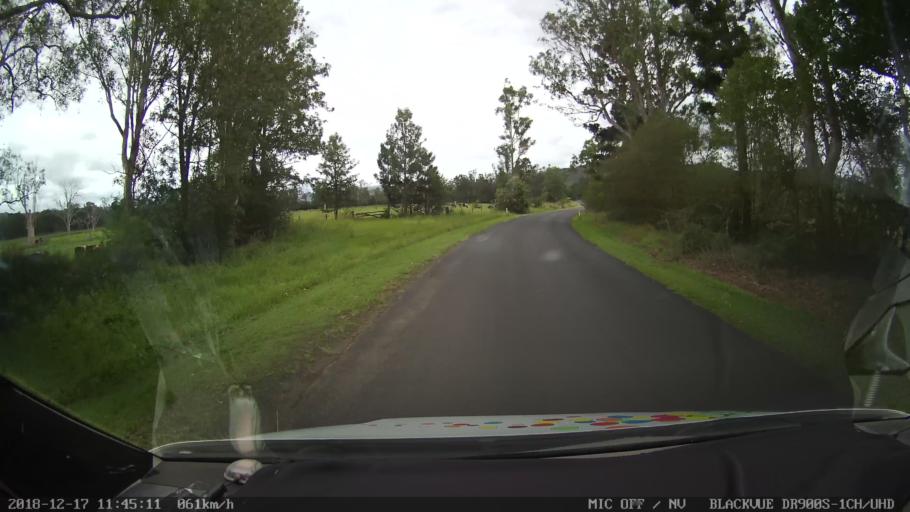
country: AU
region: New South Wales
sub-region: Kyogle
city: Kyogle
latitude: -28.6463
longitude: 152.5951
